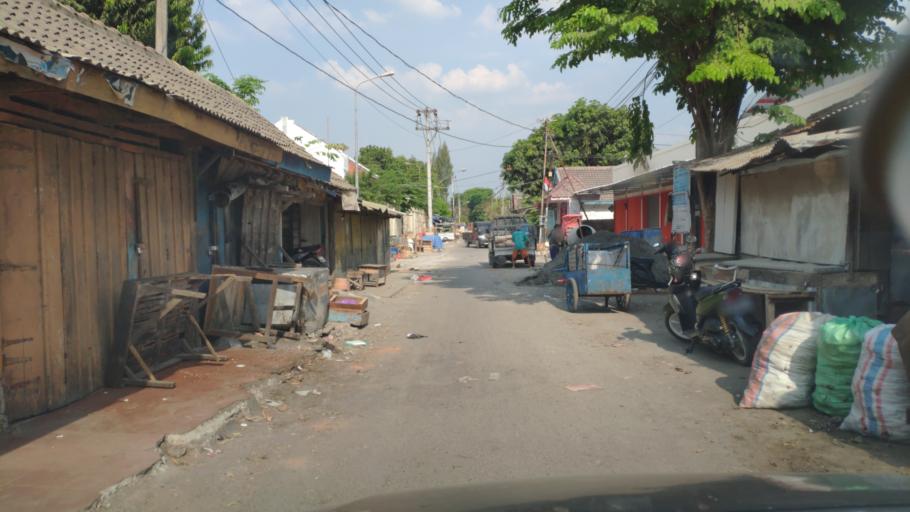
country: ID
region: Central Java
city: Cepu
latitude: -7.1432
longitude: 111.5975
